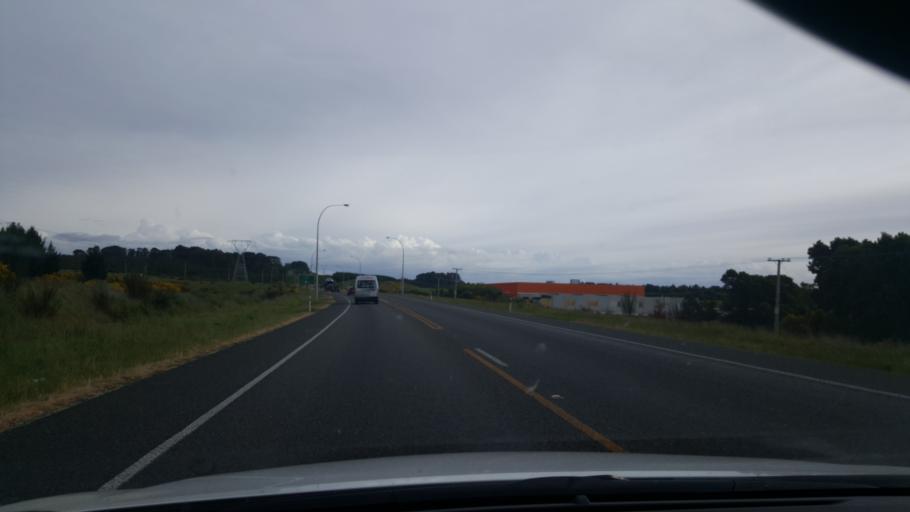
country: NZ
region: Waikato
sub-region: Taupo District
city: Taupo
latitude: -38.7005
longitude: 176.1119
